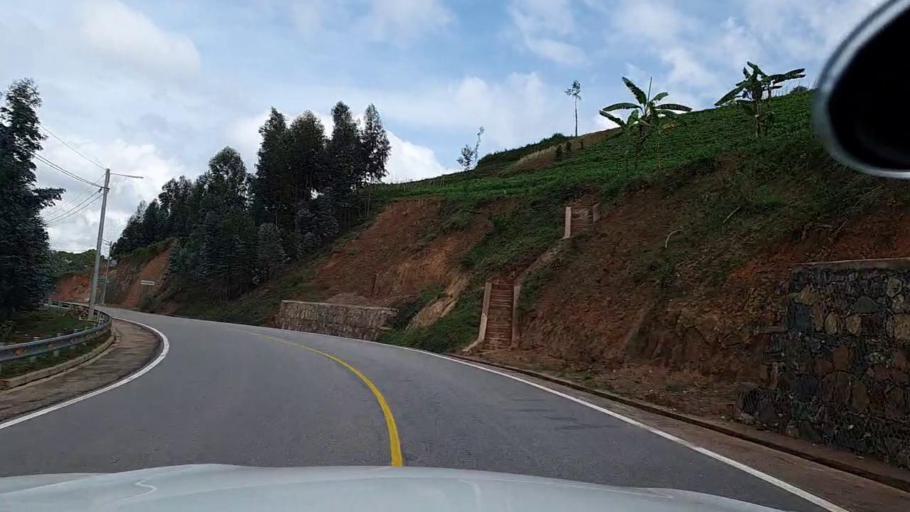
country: RW
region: Southern Province
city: Nzega
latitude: -2.5201
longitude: 29.4583
